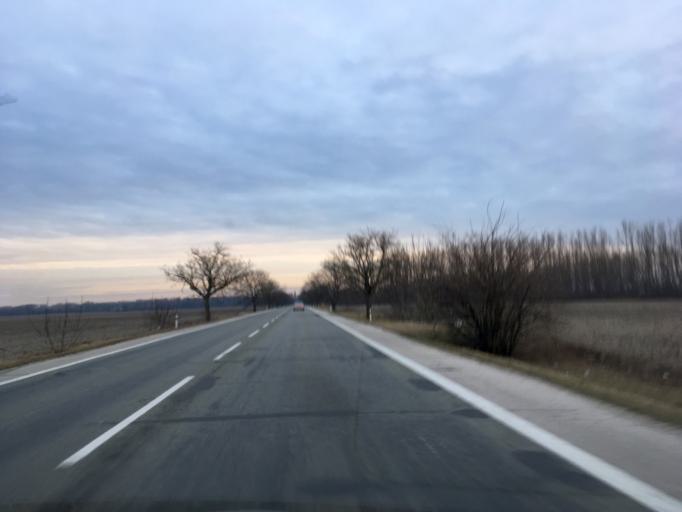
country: SK
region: Trnavsky
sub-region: Okres Dunajska Streda
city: Velky Meder
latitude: 47.9101
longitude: 17.7337
